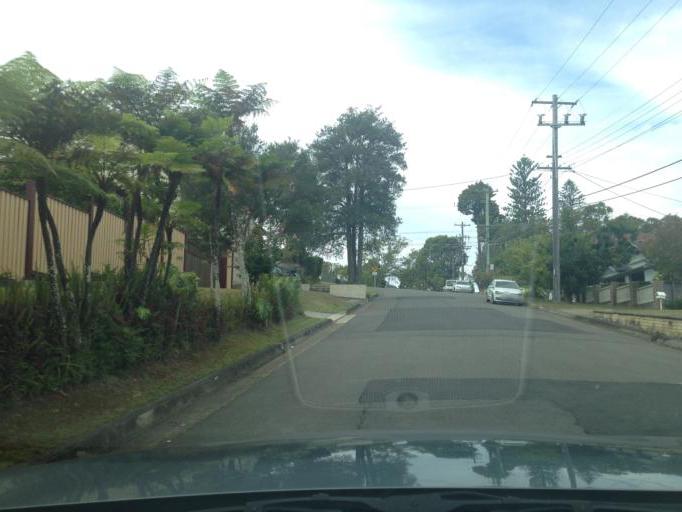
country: AU
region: New South Wales
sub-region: Ku-ring-gai
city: Killara
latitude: -33.7661
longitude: 151.1716
